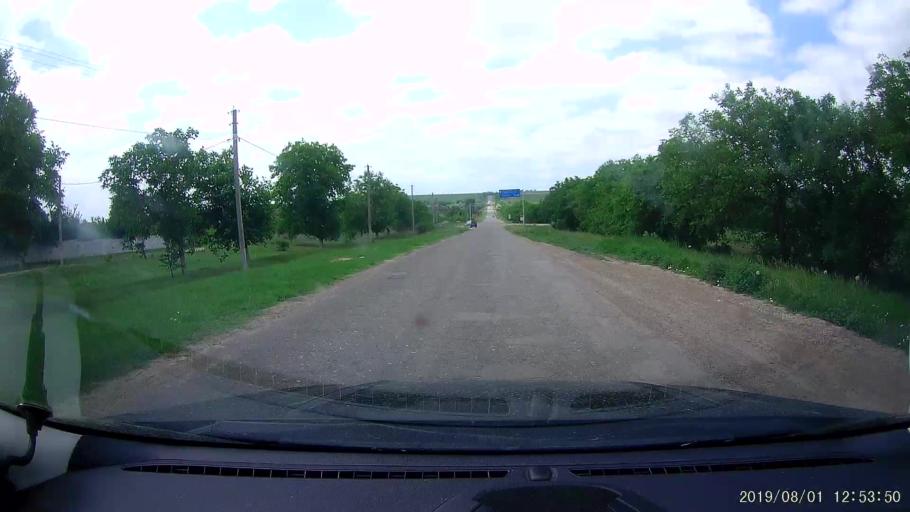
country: UA
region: Odessa
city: Vynohradivka
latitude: 45.6976
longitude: 28.4971
